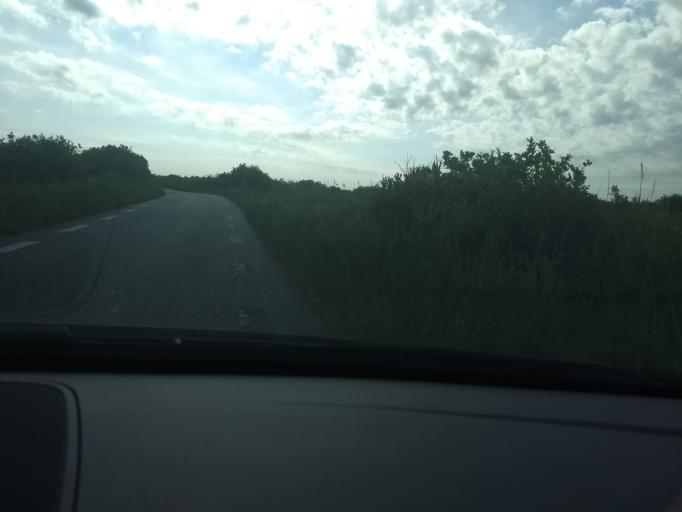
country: DE
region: Schleswig-Holstein
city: List
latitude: 55.1311
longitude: 8.5067
